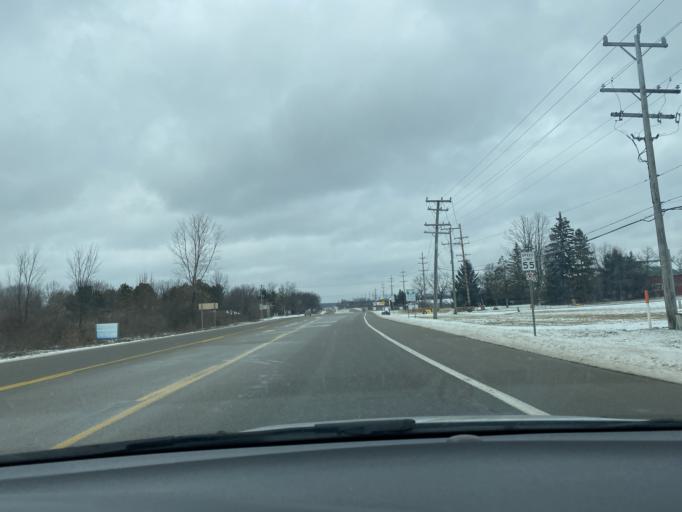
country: US
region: Michigan
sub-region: Lapeer County
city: Lapeer
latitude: 42.9565
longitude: -83.3140
